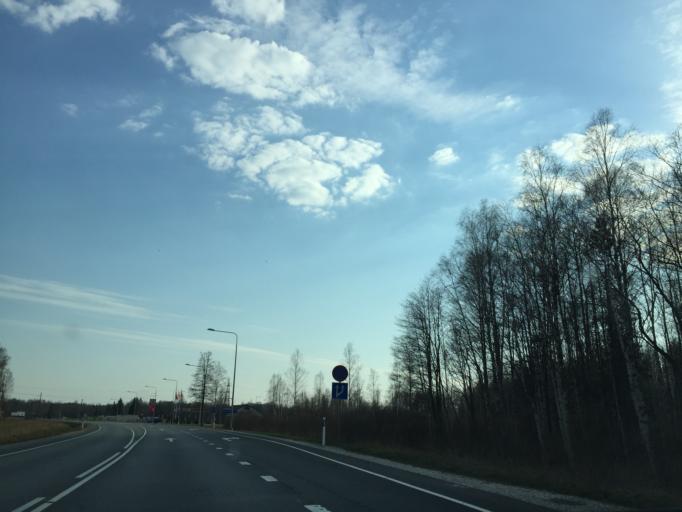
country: EE
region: Jogevamaa
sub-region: Mustvee linn
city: Mustvee
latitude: 58.8528
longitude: 26.9145
